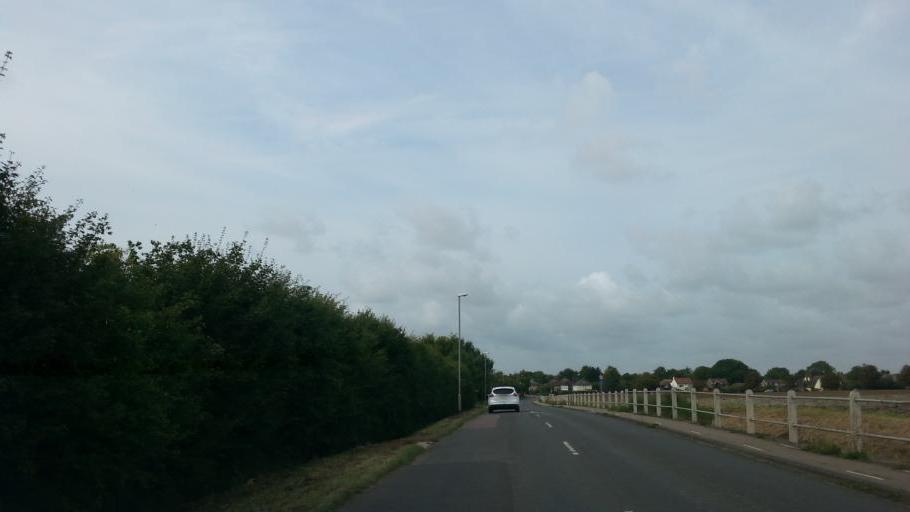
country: GB
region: England
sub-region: Cambridgeshire
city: Comberton
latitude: 52.1875
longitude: 0.0349
